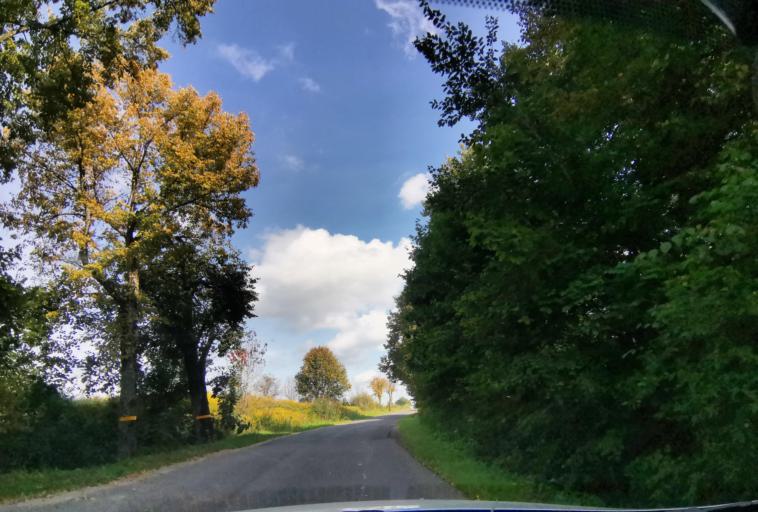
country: RU
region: Kaliningrad
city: Chernyakhovsk
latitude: 54.6595
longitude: 21.9445
